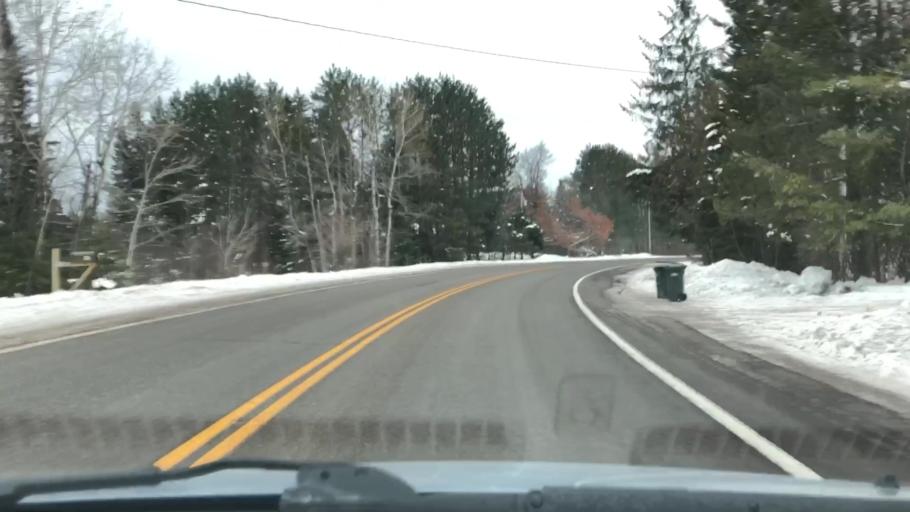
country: US
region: Minnesota
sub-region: Carlton County
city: Esko
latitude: 46.6847
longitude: -92.3650
